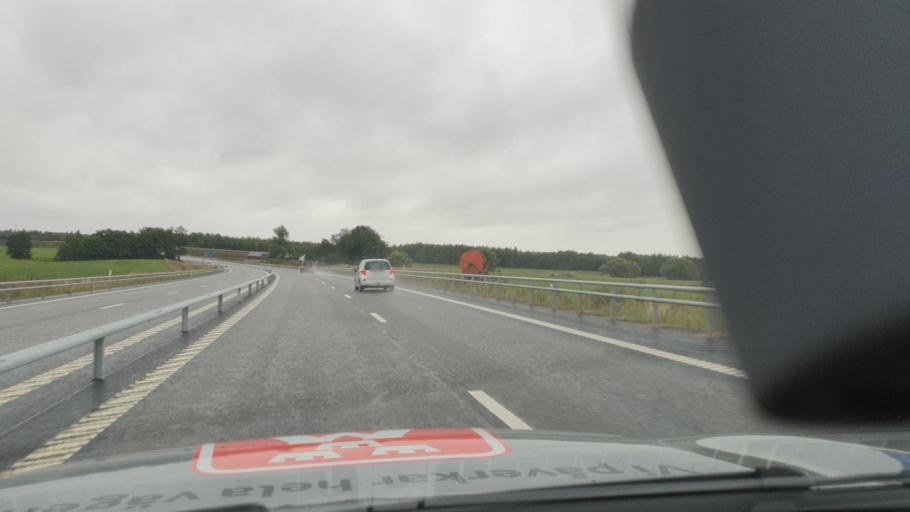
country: SE
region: Skane
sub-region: Kristianstads Kommun
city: Norra Asum
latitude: 55.9705
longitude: 14.0623
